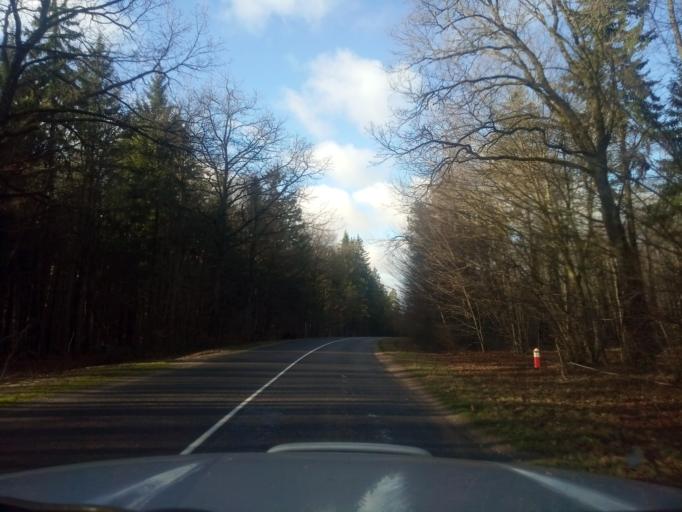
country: BY
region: Minsk
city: Kapyl'
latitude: 53.1749
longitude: 27.0147
